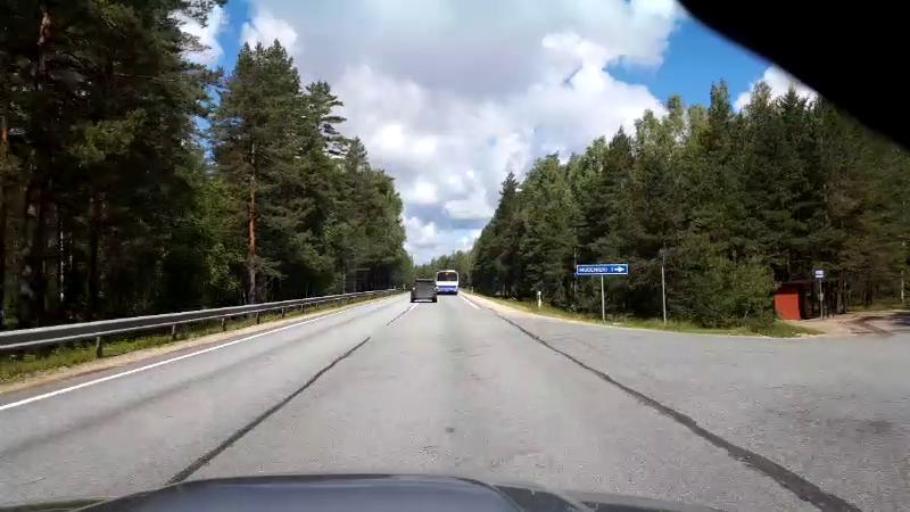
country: LV
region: Riga
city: Bergi
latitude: 56.9610
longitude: 24.3736
